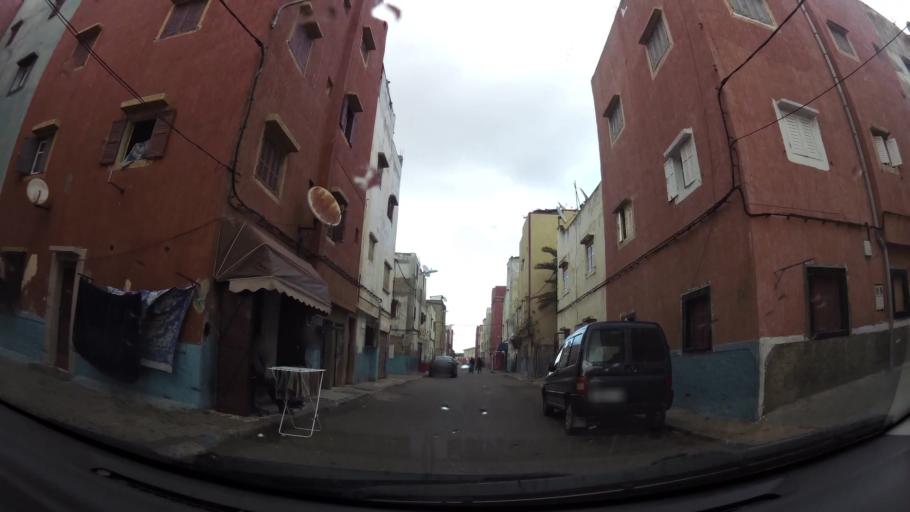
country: MA
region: Grand Casablanca
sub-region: Casablanca
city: Casablanca
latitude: 33.5576
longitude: -7.6909
